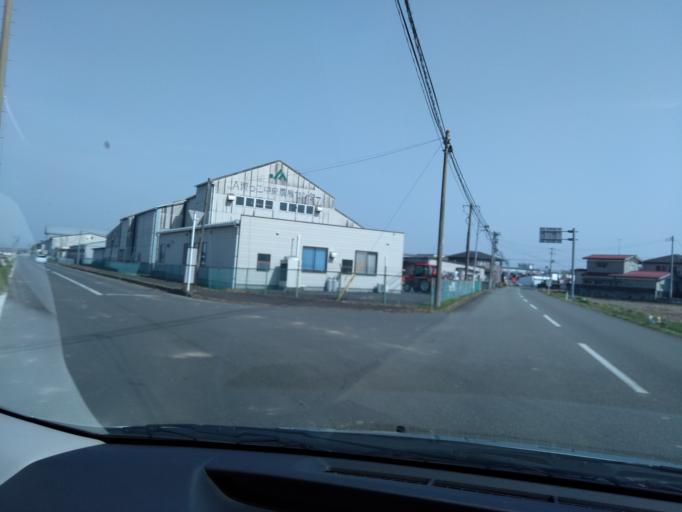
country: JP
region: Iwate
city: Ichinoseki
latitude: 38.7558
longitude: 141.0643
